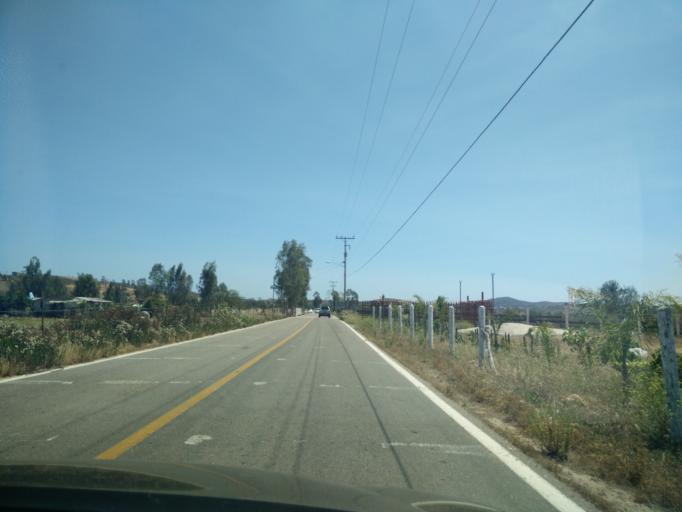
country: MX
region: Baja California
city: El Sauzal
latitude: 32.0250
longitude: -116.6739
